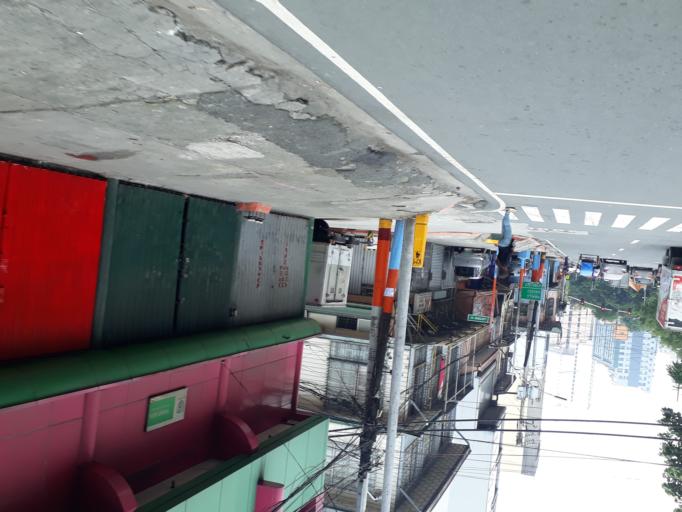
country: PH
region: Metro Manila
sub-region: City of Manila
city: Manila
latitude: 14.6095
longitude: 120.9757
